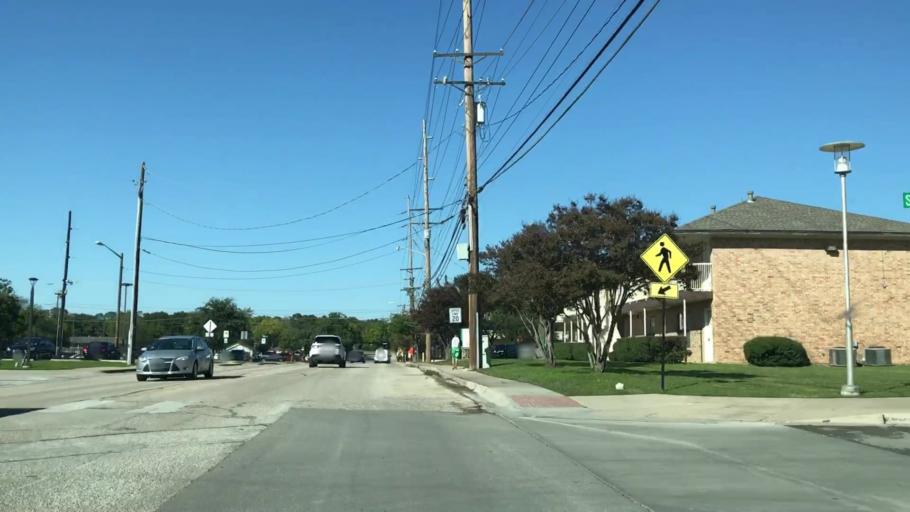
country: US
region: Texas
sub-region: Denton County
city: Denton
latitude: 33.2127
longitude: -97.1550
